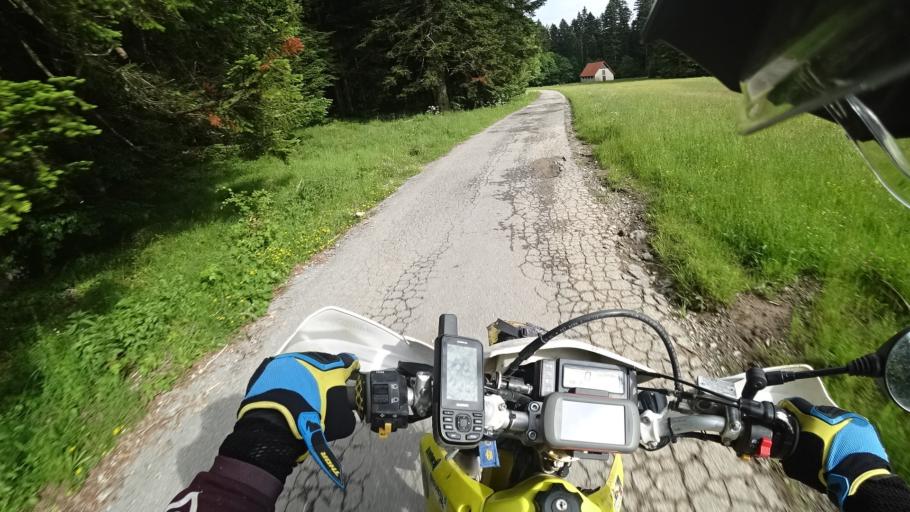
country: HR
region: Primorsko-Goranska
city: Vrbovsko
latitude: 45.2558
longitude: 14.9374
